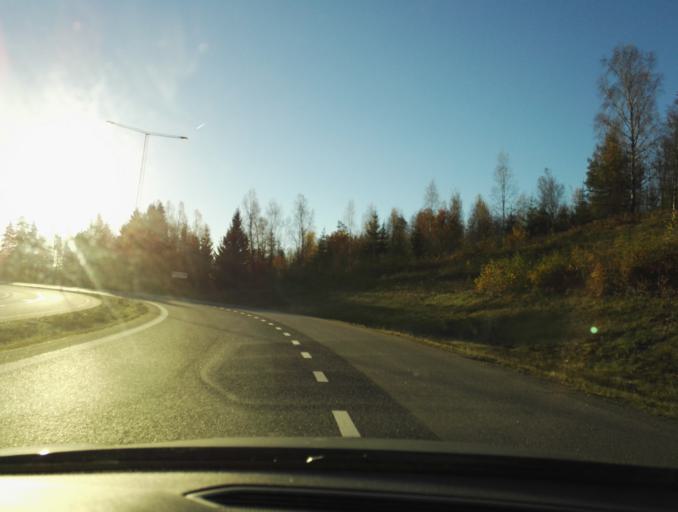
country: SE
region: Kronoberg
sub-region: Vaxjo Kommun
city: Vaexjoe
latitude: 56.8960
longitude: 14.7280
